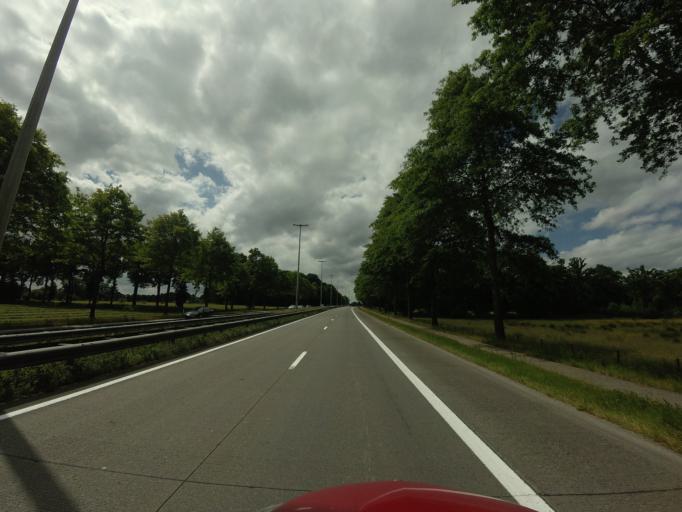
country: BE
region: Flanders
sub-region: Provincie Oost-Vlaanderen
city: Maldegem
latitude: 51.1750
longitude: 3.4472
